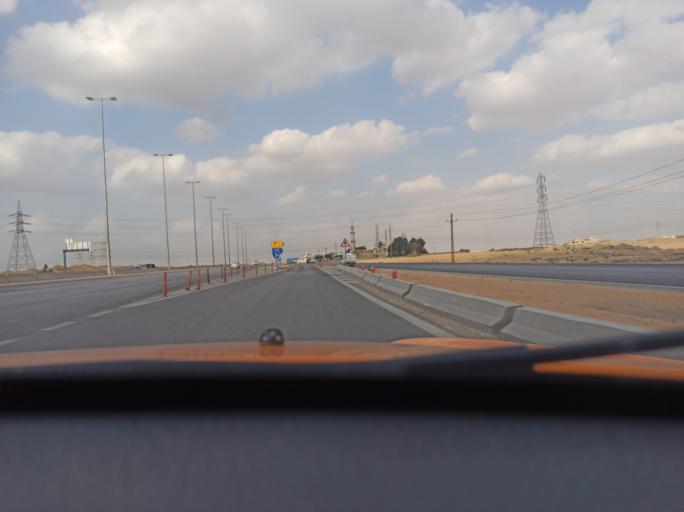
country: EG
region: Eastern Province
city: Bilbays
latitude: 30.2360
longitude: 31.7135
